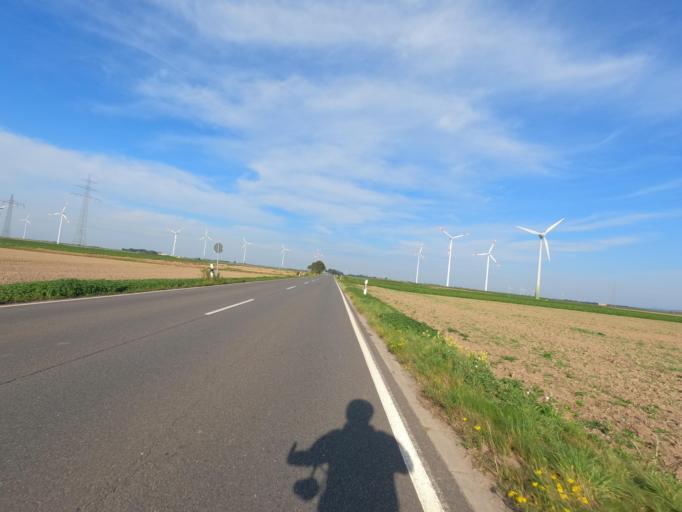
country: DE
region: North Rhine-Westphalia
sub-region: Regierungsbezirk Koln
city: Linnich
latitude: 50.9851
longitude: 6.2418
